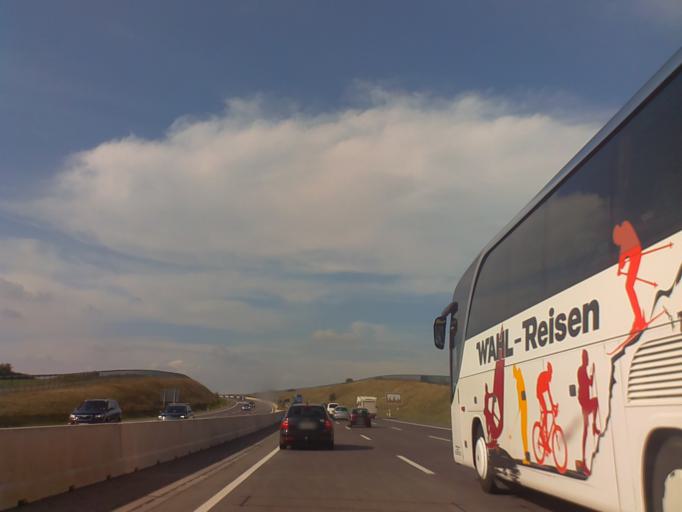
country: DE
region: Thuringia
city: Haina
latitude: 50.9806
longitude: 10.4819
